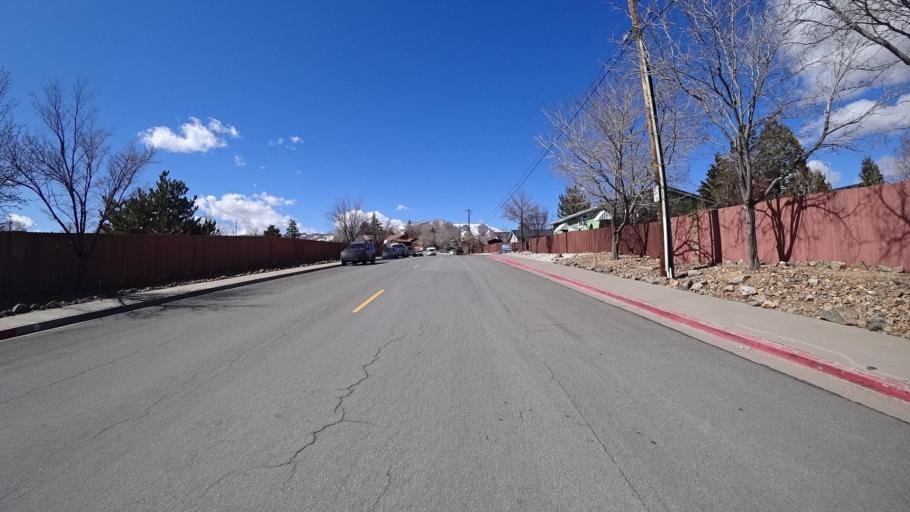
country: US
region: Nevada
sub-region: Washoe County
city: Golden Valley
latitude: 39.5926
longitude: -119.8370
